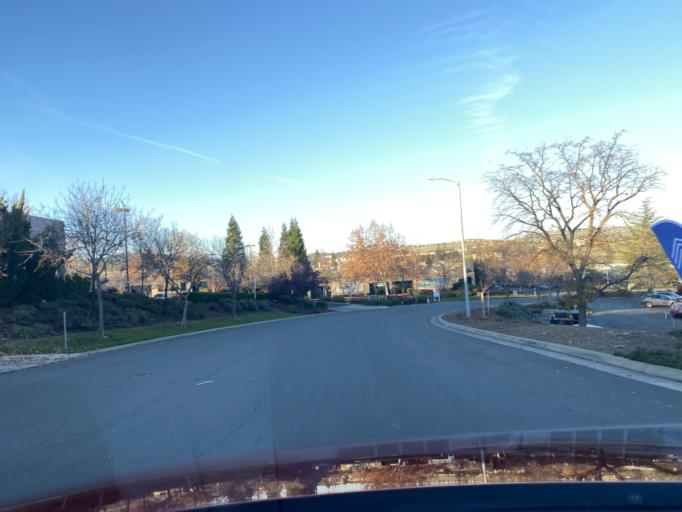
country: US
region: California
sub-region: El Dorado County
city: El Dorado Hills
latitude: 38.6393
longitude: -121.0712
